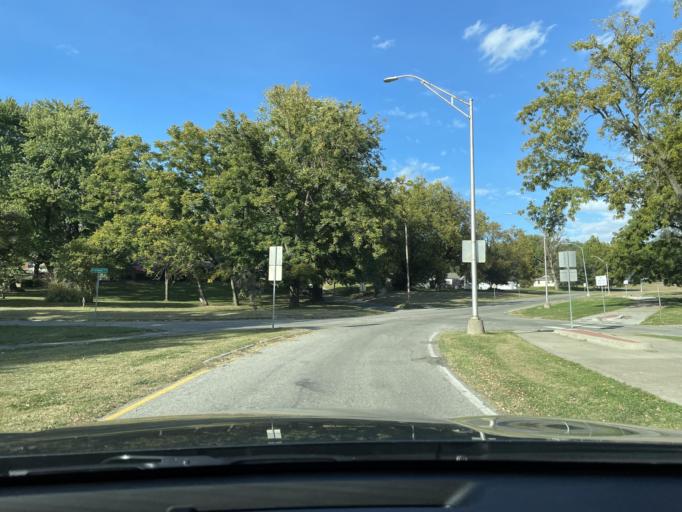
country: US
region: Kansas
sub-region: Doniphan County
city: Elwood
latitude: 39.7166
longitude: -94.8555
